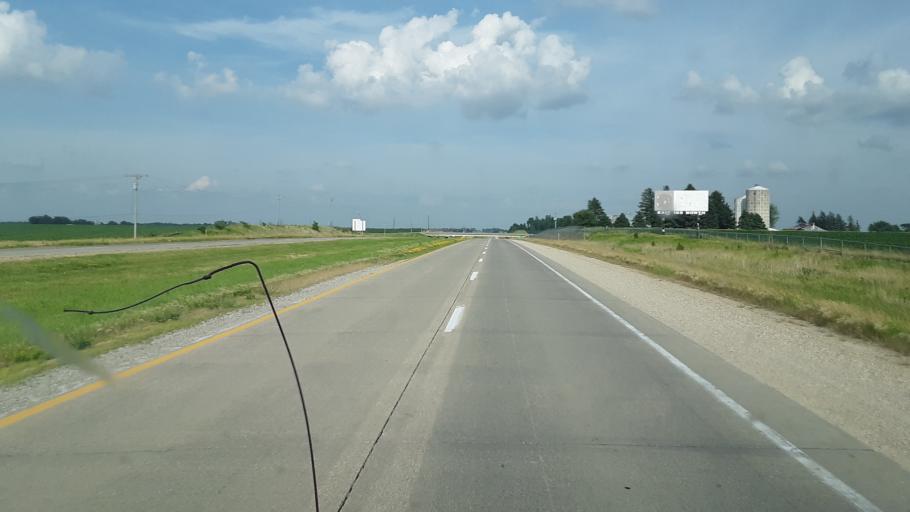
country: US
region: Iowa
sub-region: Marshall County
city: Marshalltown
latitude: 42.0077
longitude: -93.0071
